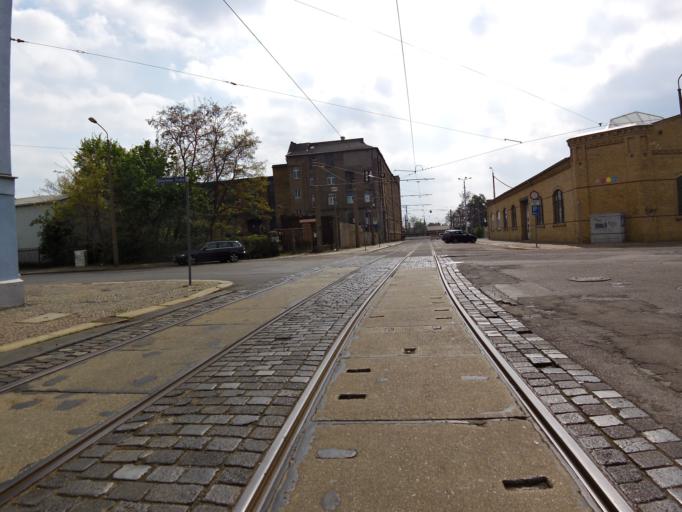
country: DE
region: Saxony
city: Leipzig
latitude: 51.3561
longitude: 12.3892
